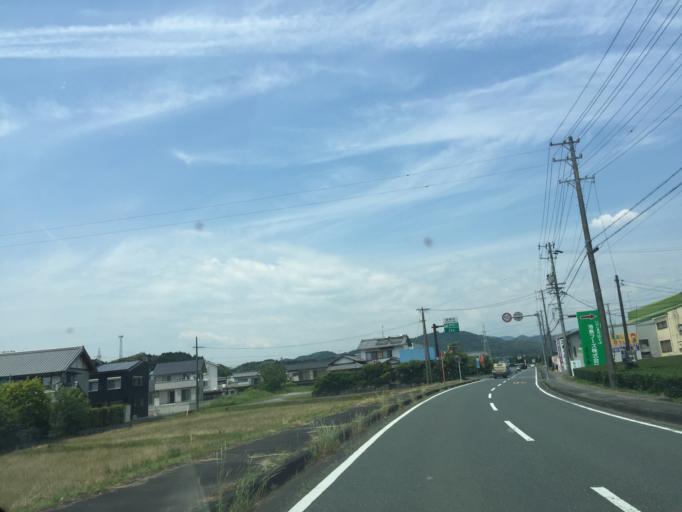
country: JP
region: Shizuoka
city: Mori
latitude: 34.8128
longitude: 137.9551
